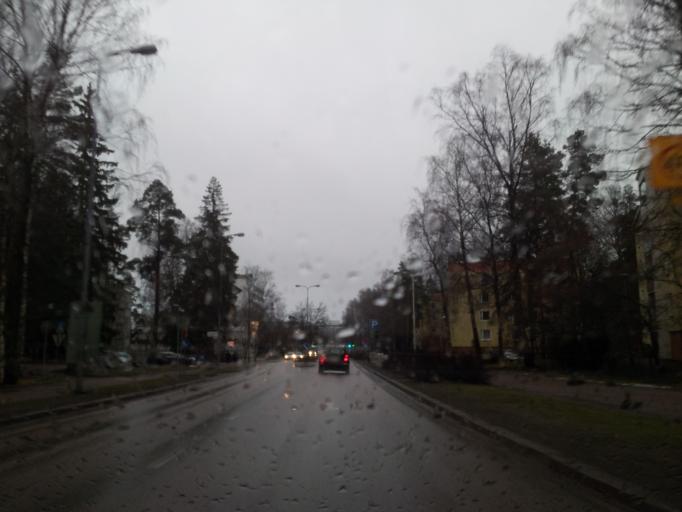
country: FI
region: Uusimaa
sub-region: Helsinki
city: Otaniemi
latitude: 60.1780
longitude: 24.7988
